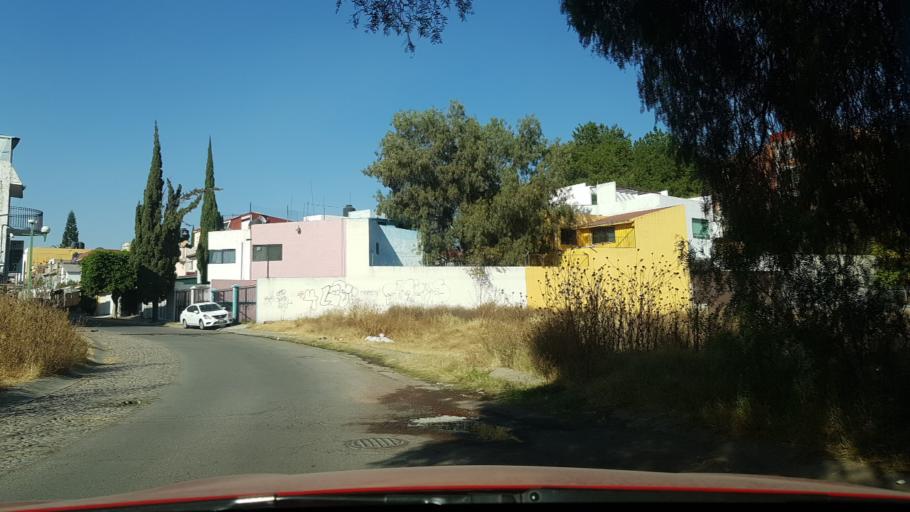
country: MX
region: Mexico
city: Cuautitlan Izcalli
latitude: 19.6384
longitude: -99.1978
